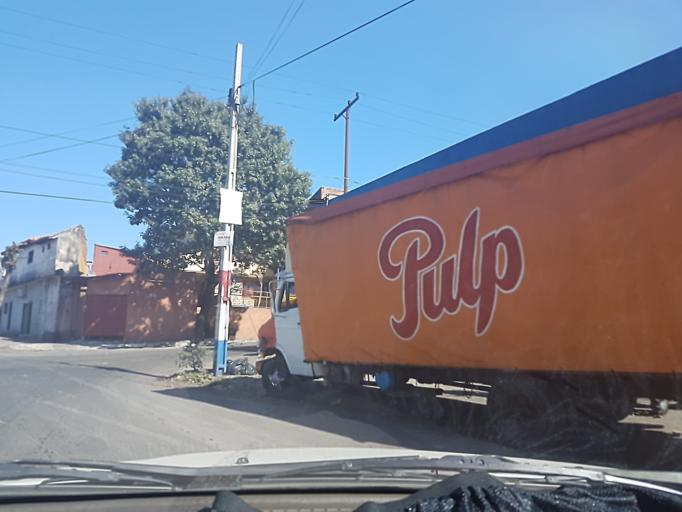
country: PY
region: Asuncion
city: Asuncion
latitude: -25.3031
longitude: -57.6259
